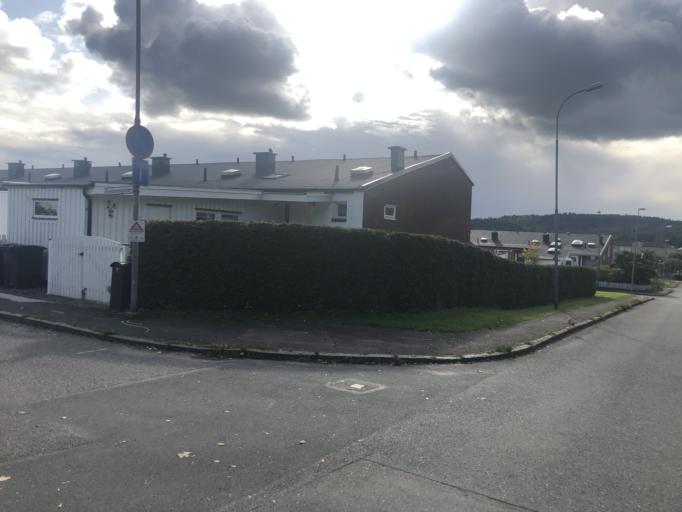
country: SE
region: Vaestra Goetaland
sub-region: Molndal
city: Moelndal
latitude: 57.6499
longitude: 12.0057
